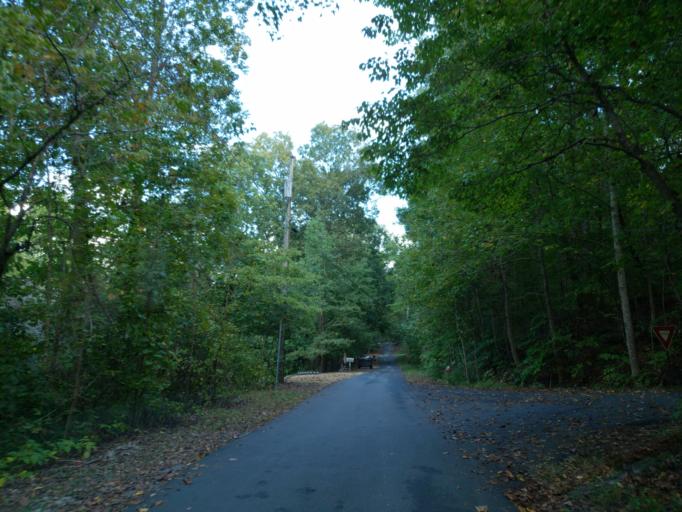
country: US
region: Georgia
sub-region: Fulton County
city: Roswell
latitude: 34.0841
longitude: -84.4082
